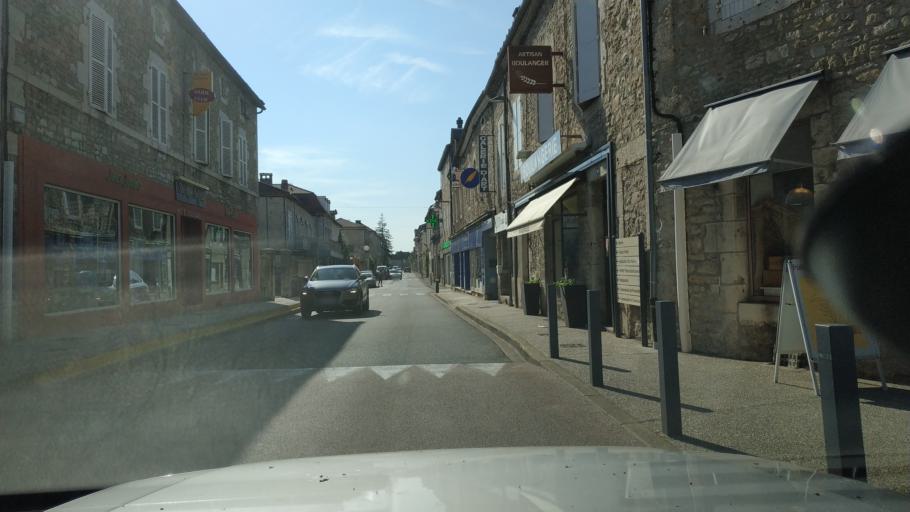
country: FR
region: Midi-Pyrenees
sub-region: Departement du Lot
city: Gramat
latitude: 44.7800
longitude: 1.7253
